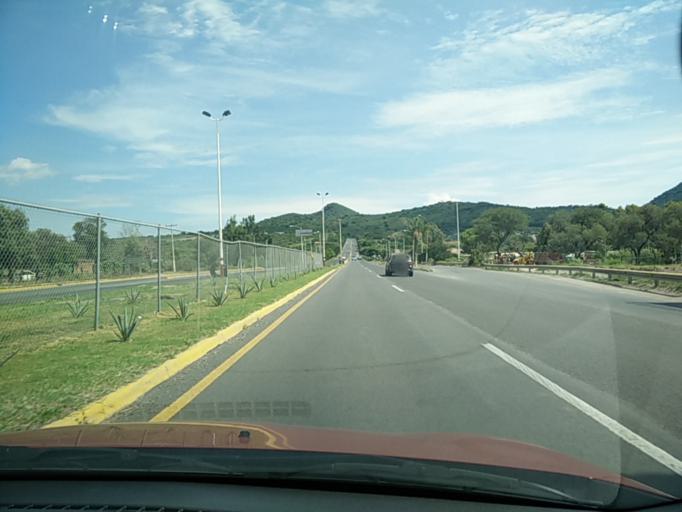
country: MX
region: Jalisco
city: Ixtlahuacan de los Membrillos
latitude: 20.3533
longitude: -103.1908
